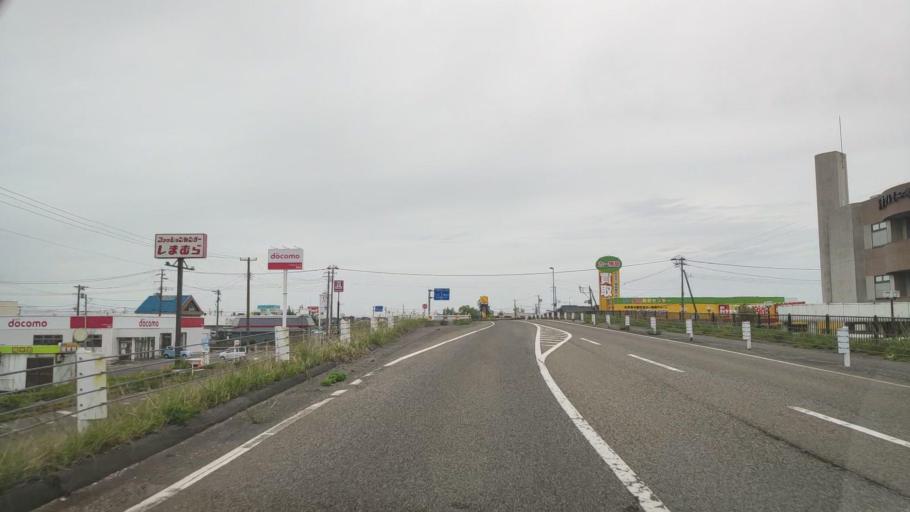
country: JP
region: Niigata
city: Niitsu-honcho
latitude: 37.7904
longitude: 139.1112
